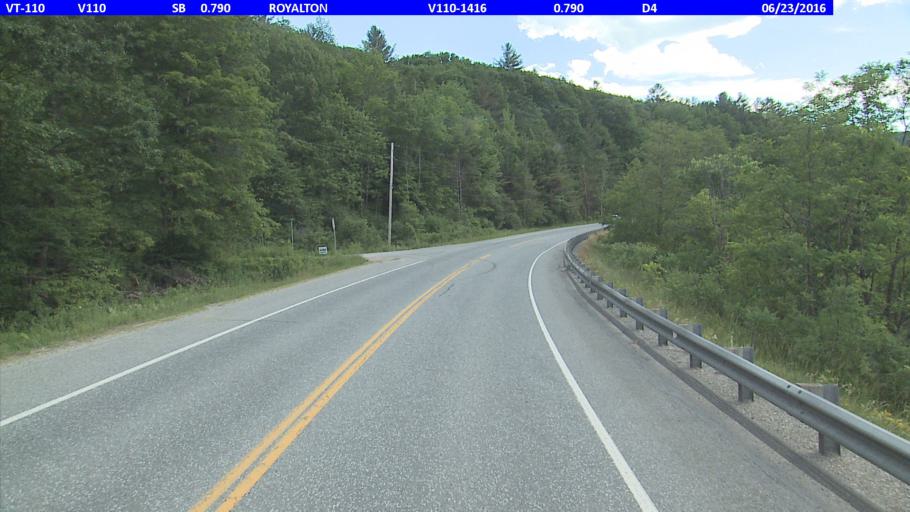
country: US
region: Vermont
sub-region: Orange County
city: Chelsea
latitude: 43.8335
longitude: -72.5117
